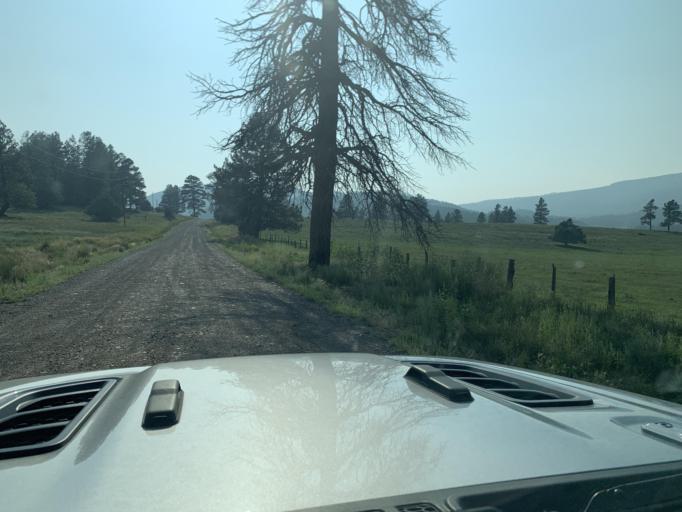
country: US
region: Colorado
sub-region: Archuleta County
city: Pagosa Springs
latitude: 37.2235
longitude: -107.2064
